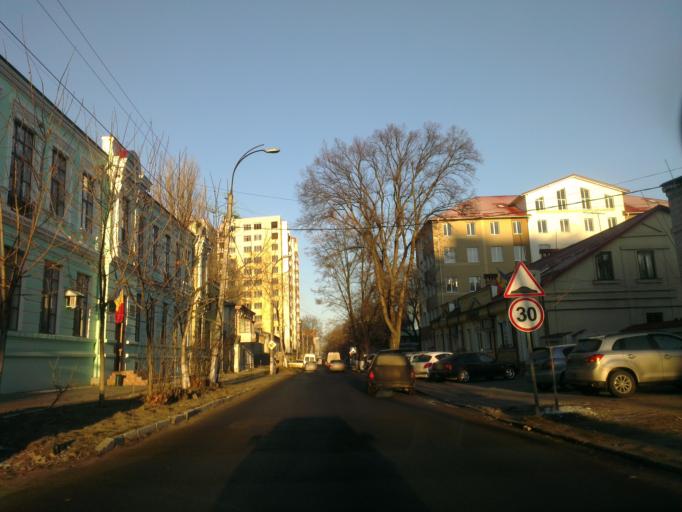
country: MD
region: Chisinau
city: Chisinau
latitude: 47.0308
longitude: 28.8321
